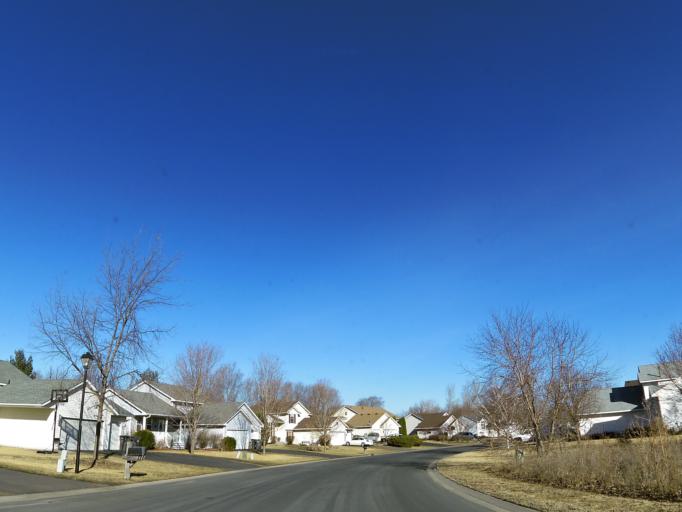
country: US
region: Minnesota
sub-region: Scott County
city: Savage
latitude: 44.7723
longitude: -93.3975
